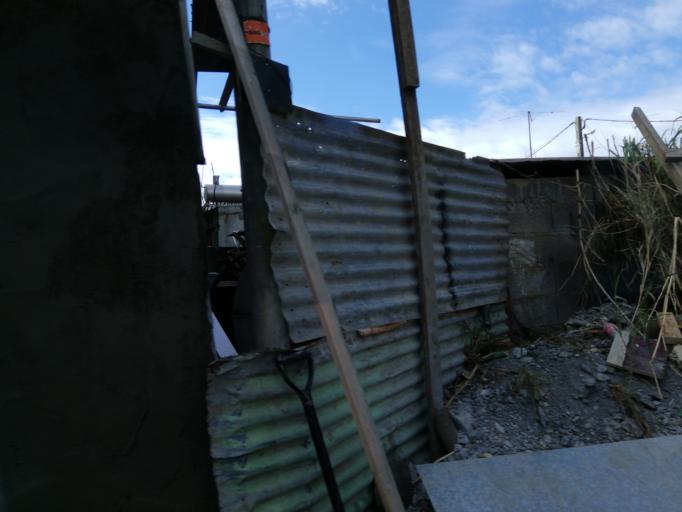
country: MU
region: Black River
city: Petite Riviere
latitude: -20.2242
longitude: 57.4558
